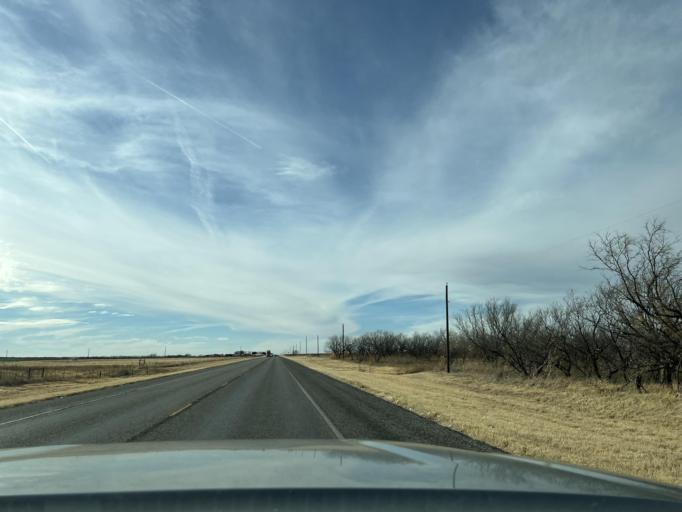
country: US
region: Texas
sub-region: Jones County
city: Anson
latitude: 32.7519
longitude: -99.9348
